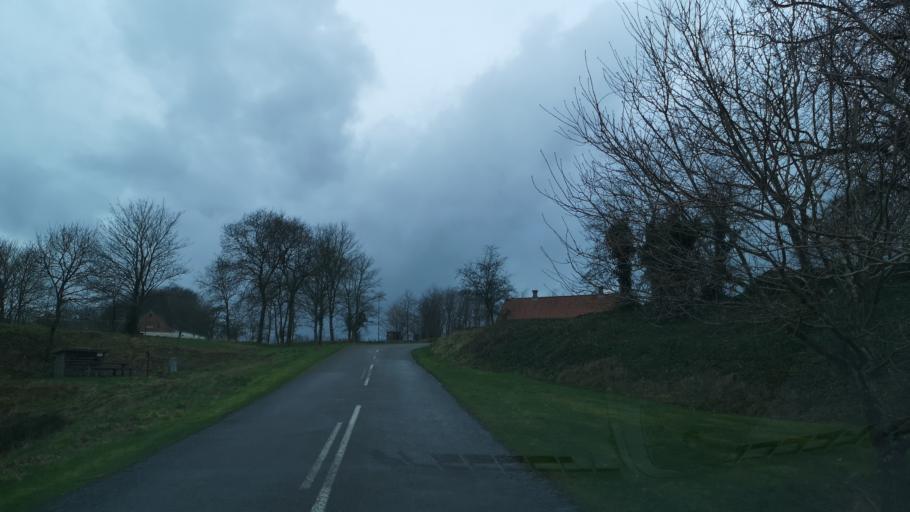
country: DK
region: Central Jutland
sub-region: Herning Kommune
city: Lind
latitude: 56.0028
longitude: 8.9685
